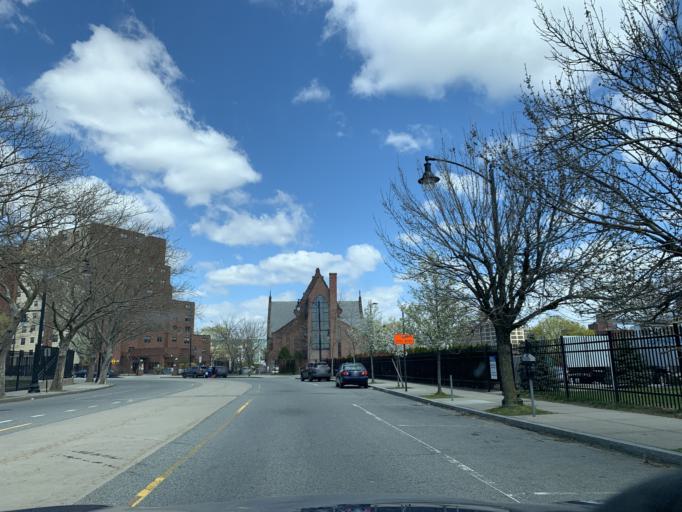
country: US
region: Rhode Island
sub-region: Providence County
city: Providence
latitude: 41.8173
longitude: -71.4181
